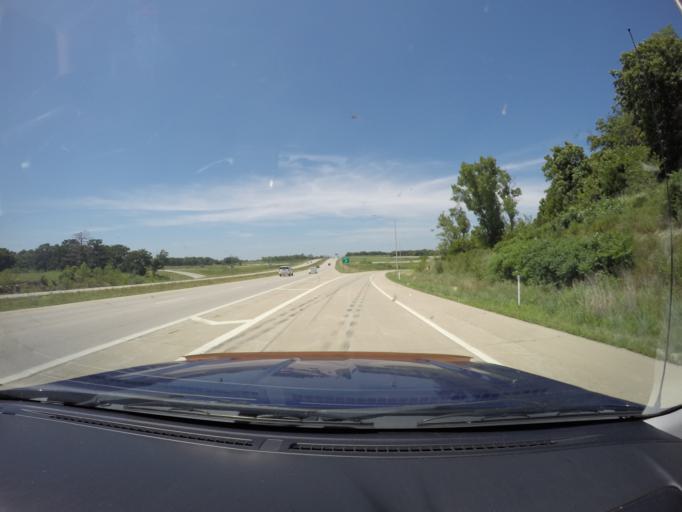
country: US
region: Kansas
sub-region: Wyandotte County
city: Bonner Springs
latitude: 39.1126
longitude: -94.8908
